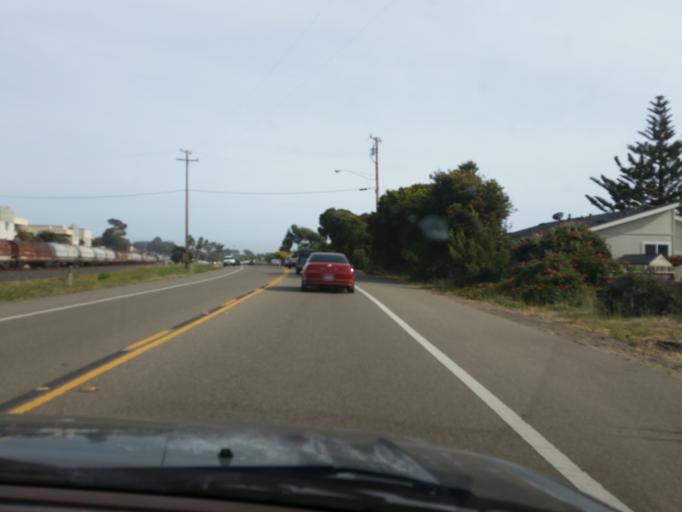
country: US
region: California
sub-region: San Luis Obispo County
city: Grover Beach
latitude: 35.1265
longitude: -120.6318
